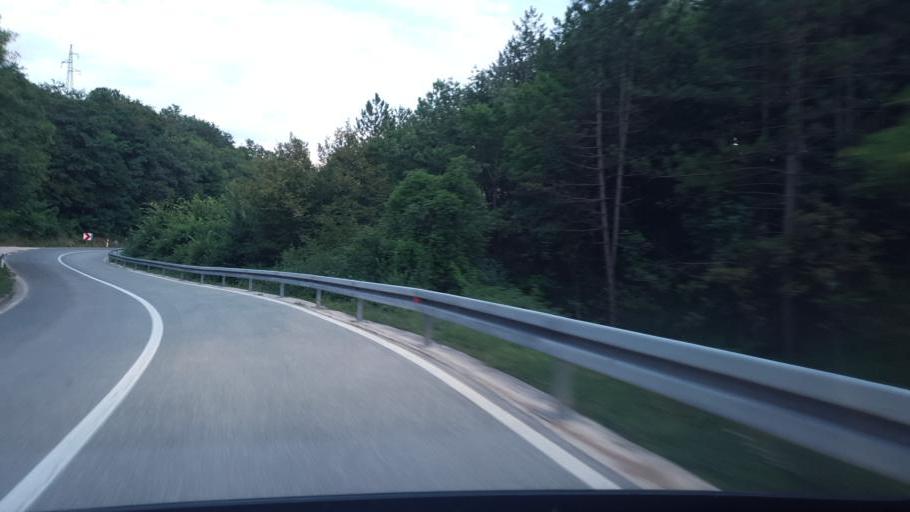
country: HR
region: Primorsko-Goranska
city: Punat
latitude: 45.0143
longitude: 14.6983
